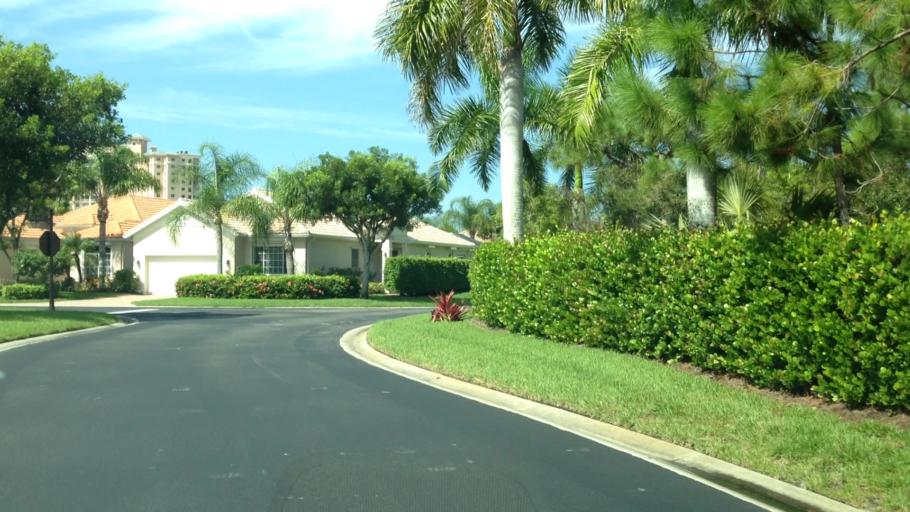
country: US
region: Florida
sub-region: Collier County
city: Naples Park
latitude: 26.3048
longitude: -81.8206
